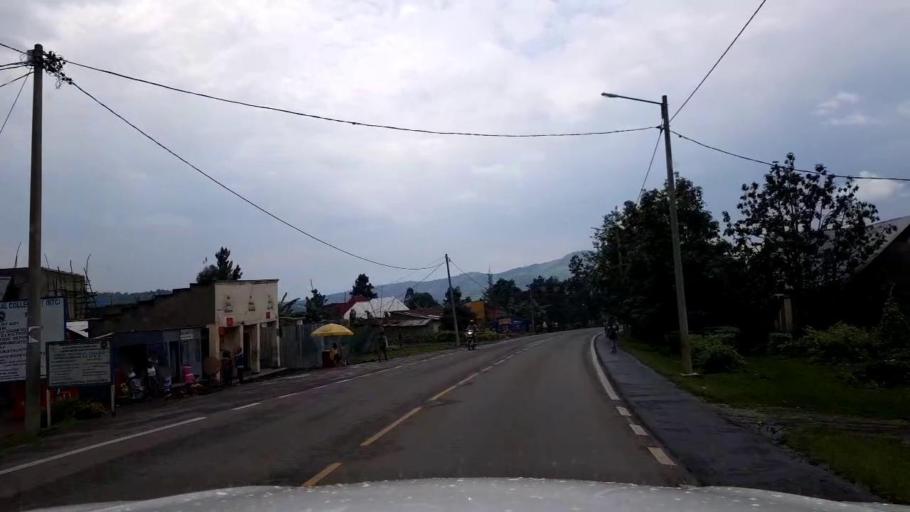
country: RW
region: Western Province
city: Gisenyi
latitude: -1.6983
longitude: 29.3123
